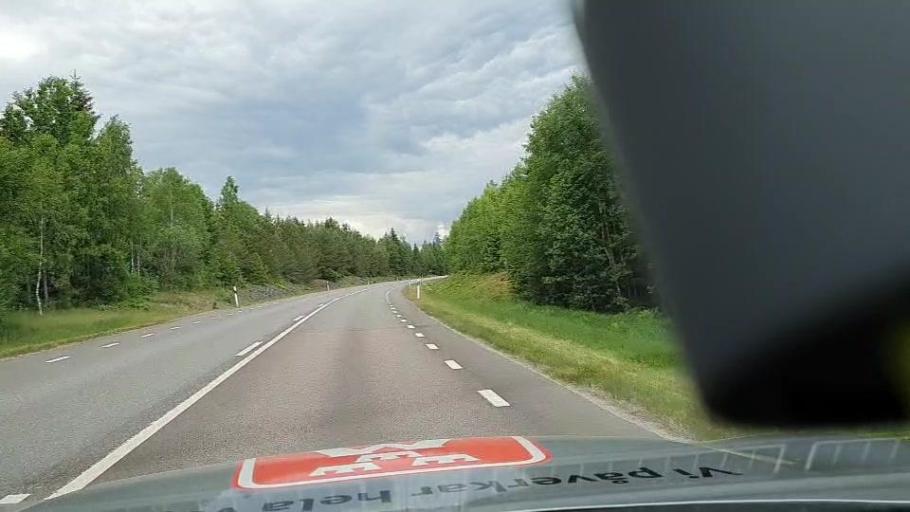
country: SE
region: Kalmar
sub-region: Emmaboda Kommun
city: Emmaboda
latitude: 56.4499
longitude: 15.5653
